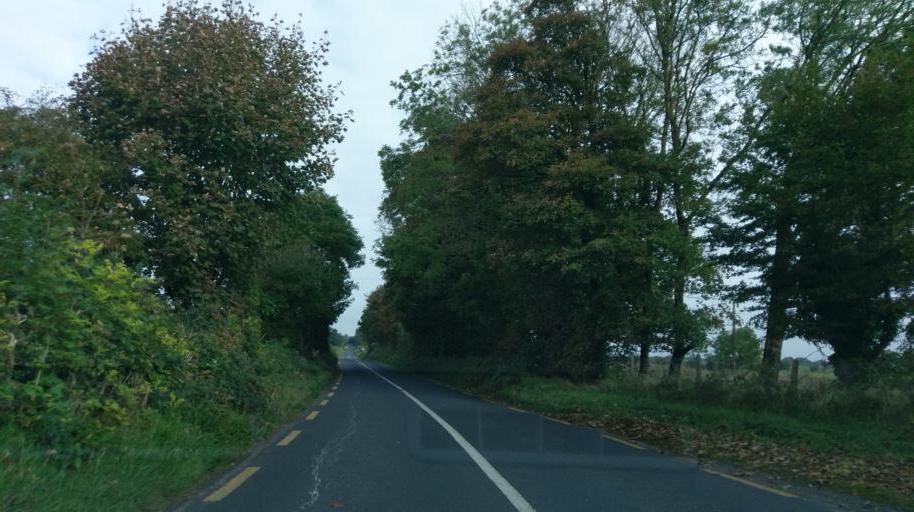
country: IE
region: Connaught
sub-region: County Galway
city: Athenry
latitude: 53.3142
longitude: -8.7324
